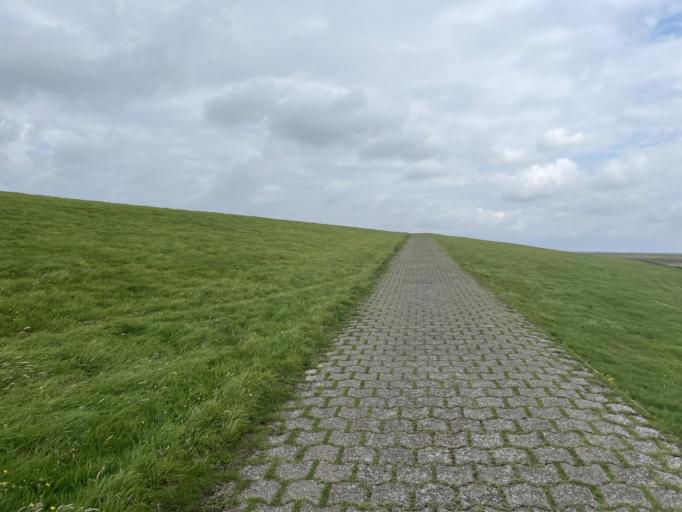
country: DE
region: Lower Saxony
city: Borkum
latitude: 53.5881
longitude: 6.7325
